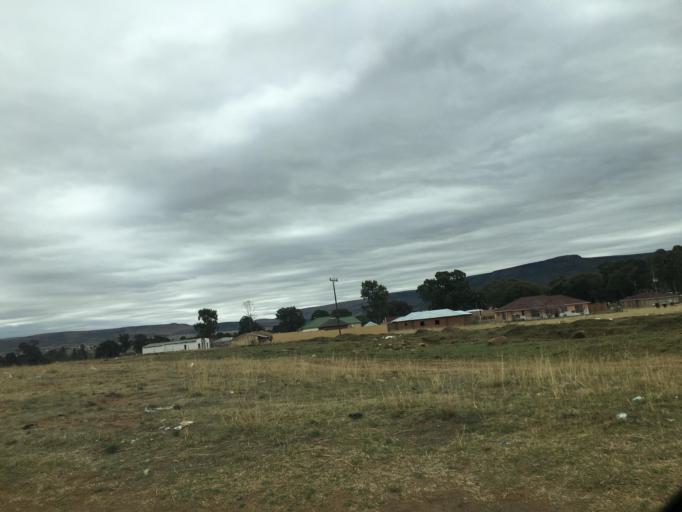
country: ZA
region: Eastern Cape
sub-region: Chris Hani District Municipality
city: Cala
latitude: -31.5327
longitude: 27.6931
